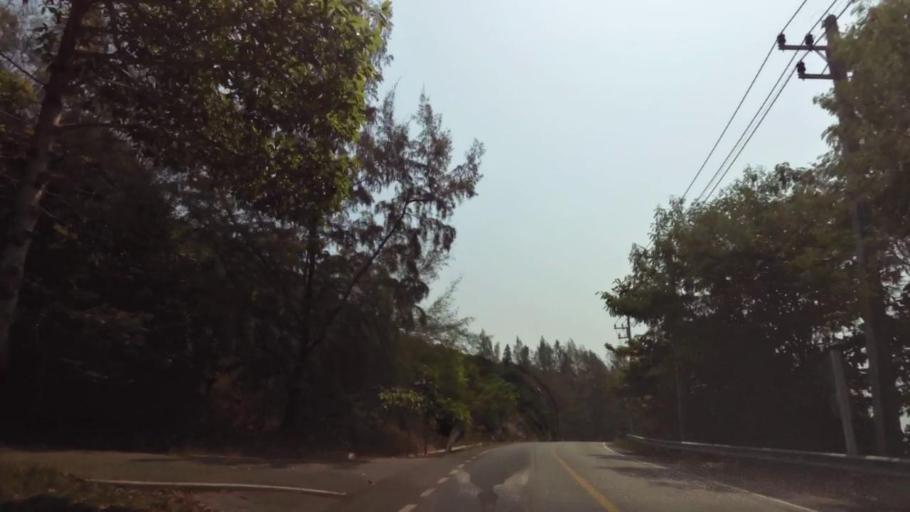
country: TH
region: Chanthaburi
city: Tha Mai
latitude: 12.5301
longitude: 101.9459
